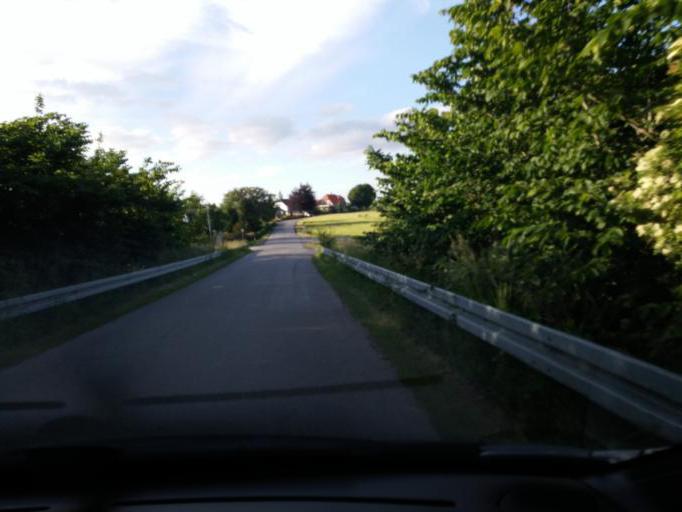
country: DK
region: South Denmark
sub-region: Kerteminde Kommune
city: Langeskov
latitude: 55.3795
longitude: 10.5207
